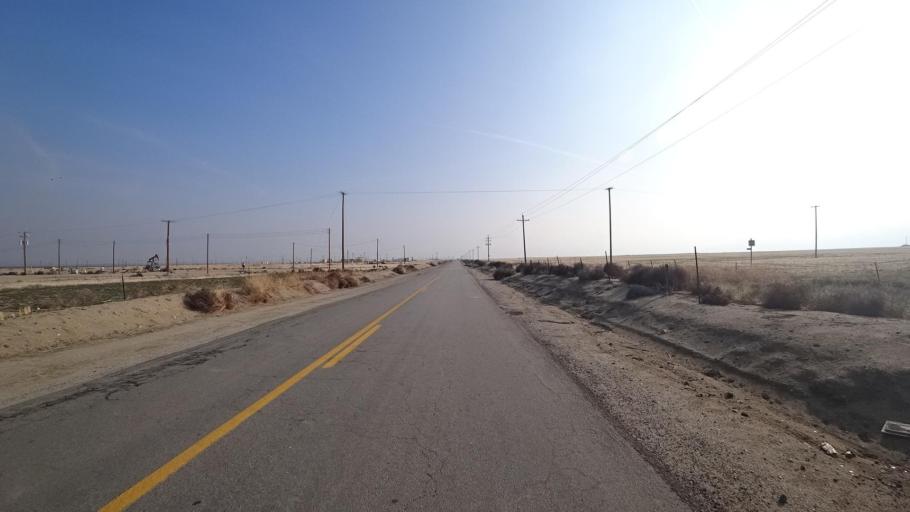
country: US
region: California
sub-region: Kern County
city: Lebec
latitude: 34.9845
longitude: -118.9353
